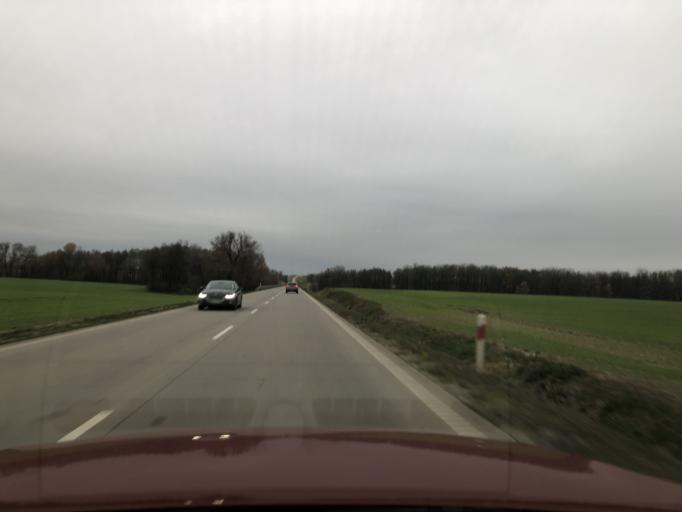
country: PL
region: Lower Silesian Voivodeship
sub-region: Powiat swidnicki
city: Swidnica
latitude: 50.8810
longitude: 16.4765
